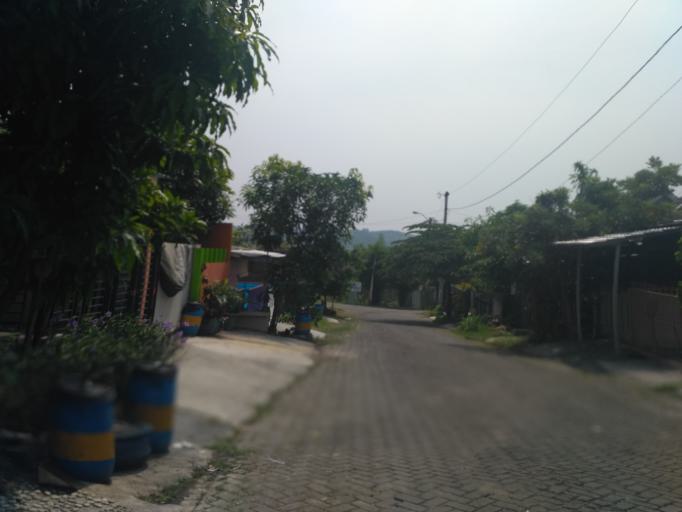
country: ID
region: Central Java
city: Mranggen
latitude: -7.0660
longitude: 110.4562
